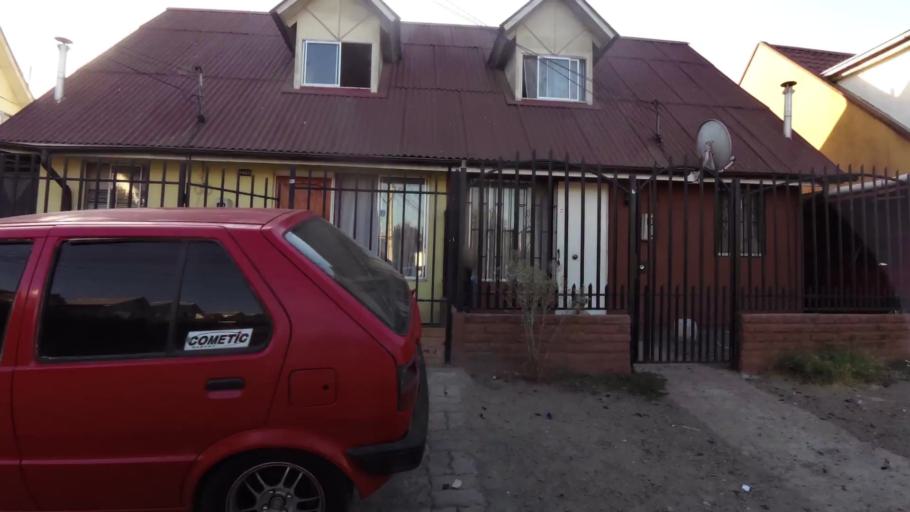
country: CL
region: Maule
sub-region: Provincia de Talca
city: Talca
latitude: -35.4506
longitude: -71.6691
